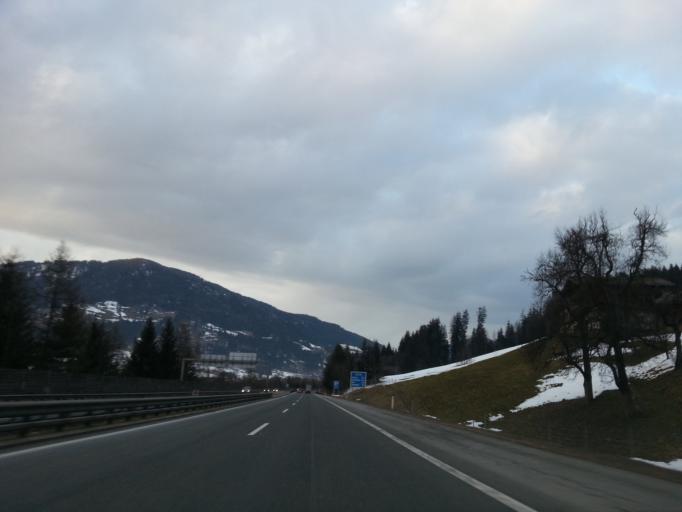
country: AT
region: Salzburg
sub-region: Politischer Bezirk Sankt Johann im Pongau
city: Flachau
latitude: 47.3635
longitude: 13.3969
